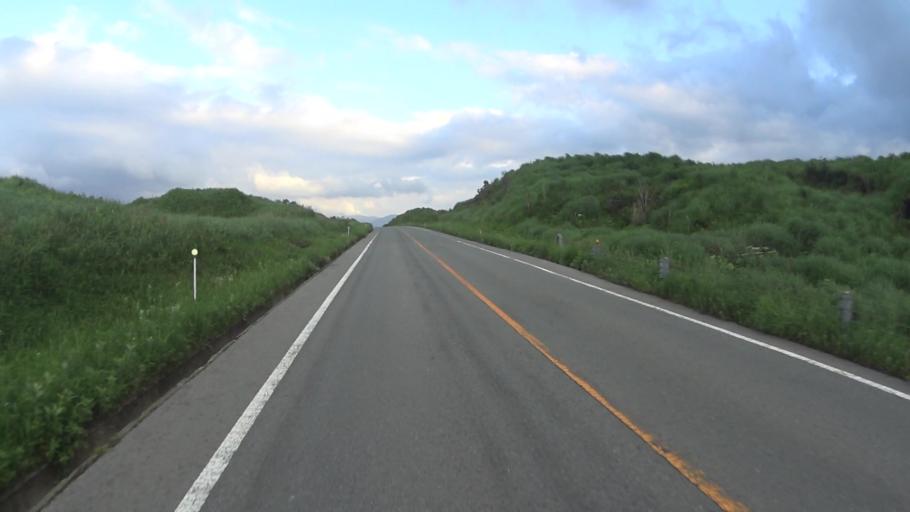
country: JP
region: Kumamoto
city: Aso
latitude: 32.9866
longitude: 131.0133
